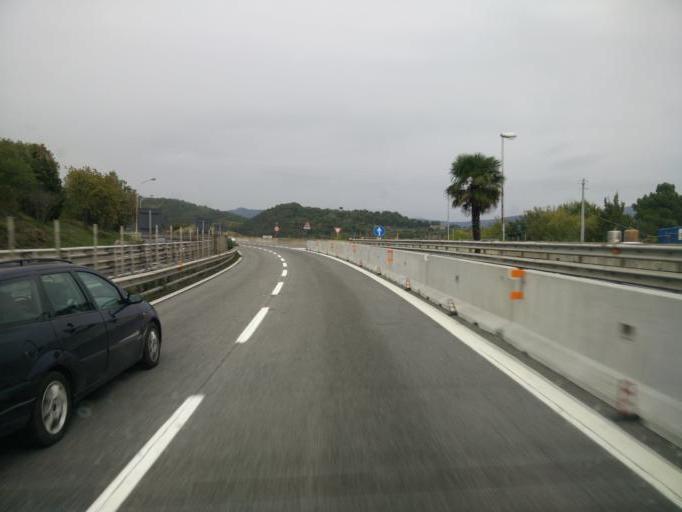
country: IT
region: Tuscany
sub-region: Province of Florence
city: Barberino di Mugello
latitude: 44.0298
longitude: 11.2257
